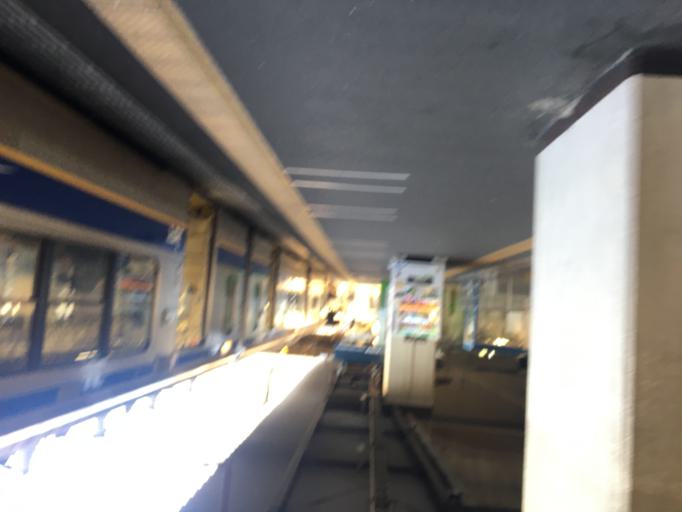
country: JP
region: Iwate
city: Morioka-shi
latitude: 39.7023
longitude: 141.1350
